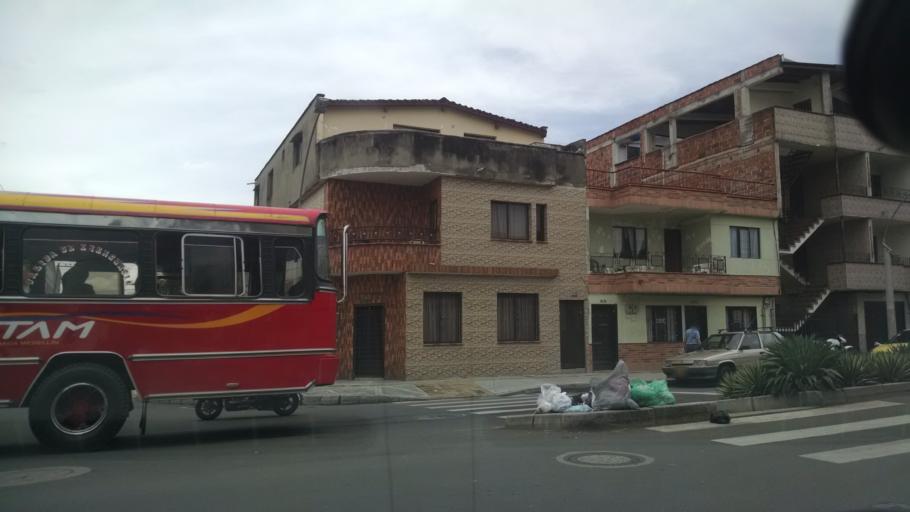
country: CO
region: Antioquia
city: Itagui
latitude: 6.2056
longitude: -75.5834
